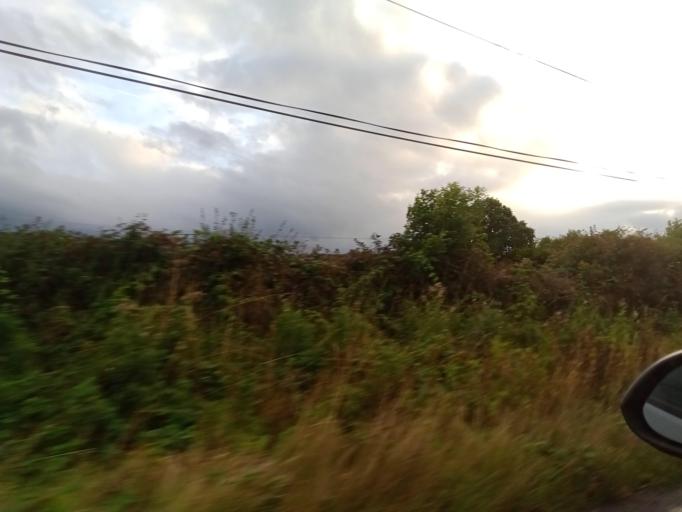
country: IE
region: Leinster
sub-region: Uibh Fhaili
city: Tullamore
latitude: 53.1451
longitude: -7.4793
